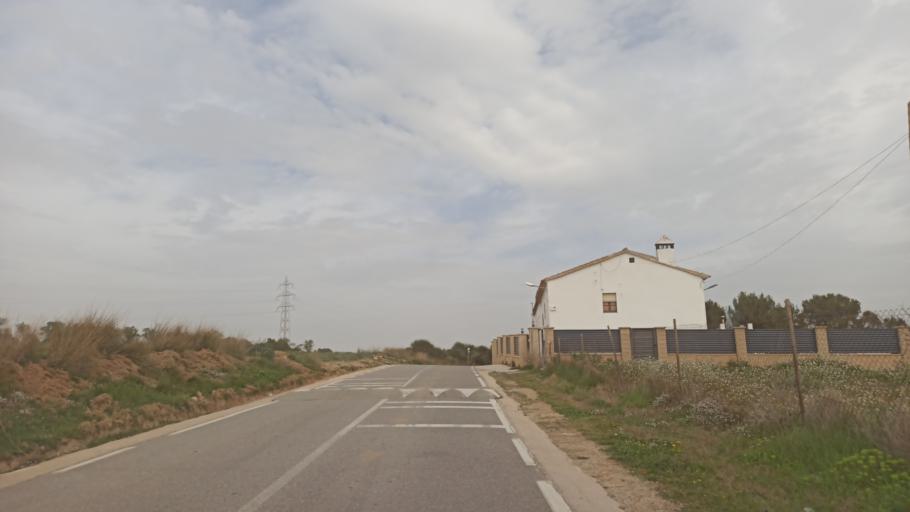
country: ES
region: Catalonia
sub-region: Provincia de Barcelona
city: Vilafranca del Penedes
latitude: 41.3253
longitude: 1.7182
